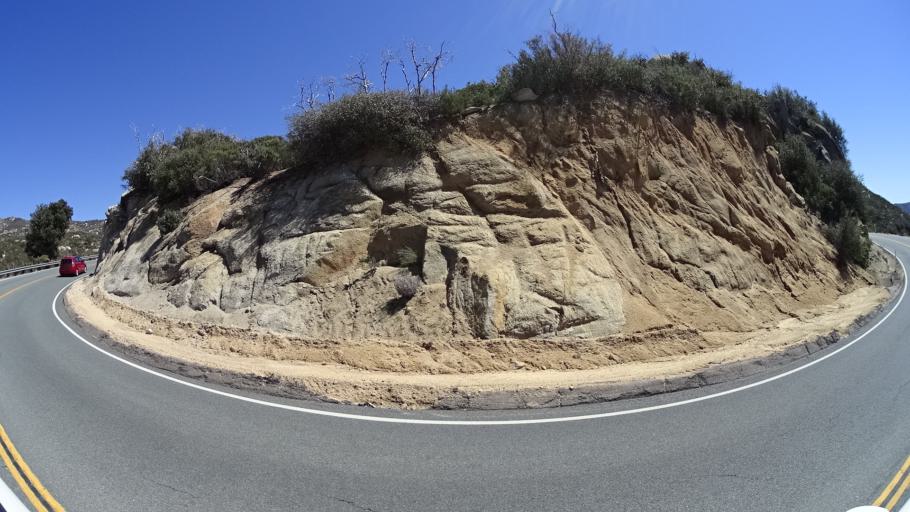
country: US
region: California
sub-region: San Diego County
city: Descanso
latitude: 32.8805
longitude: -116.5846
